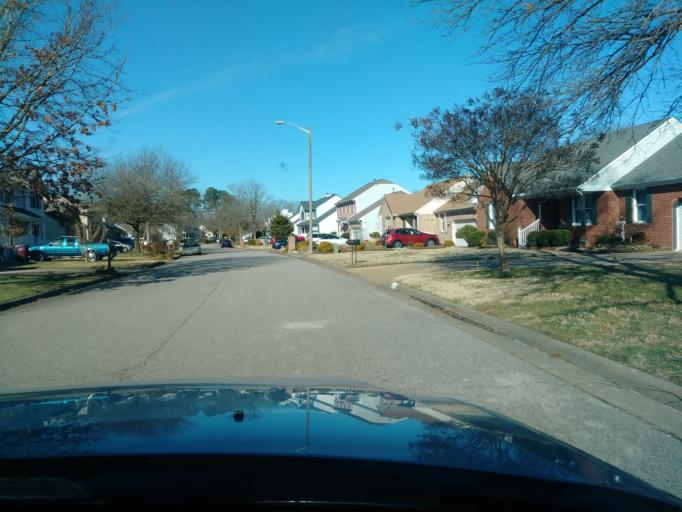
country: US
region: Virginia
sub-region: City of Chesapeake
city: Chesapeake
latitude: 36.7531
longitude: -76.2104
